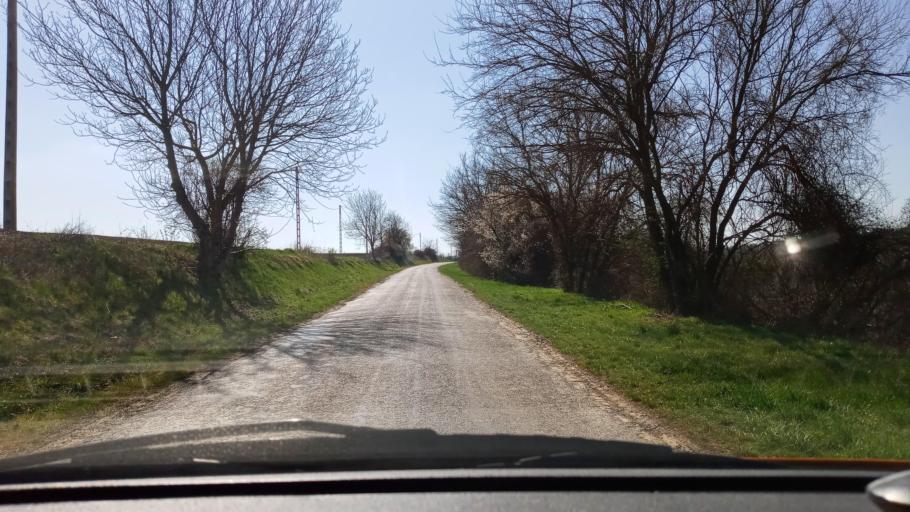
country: HU
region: Baranya
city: Kozarmisleny
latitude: 46.0411
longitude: 18.3849
